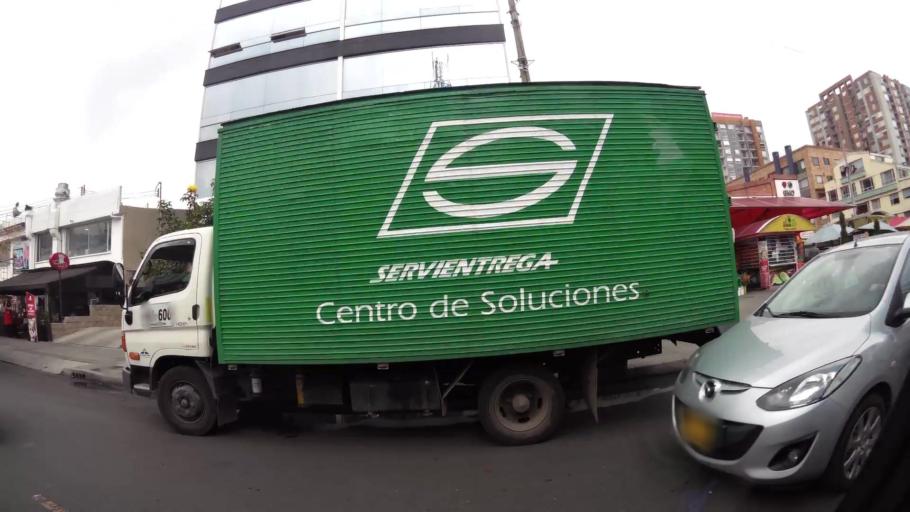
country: CO
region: Bogota D.C.
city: Barrio San Luis
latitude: 4.7204
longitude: -74.0391
